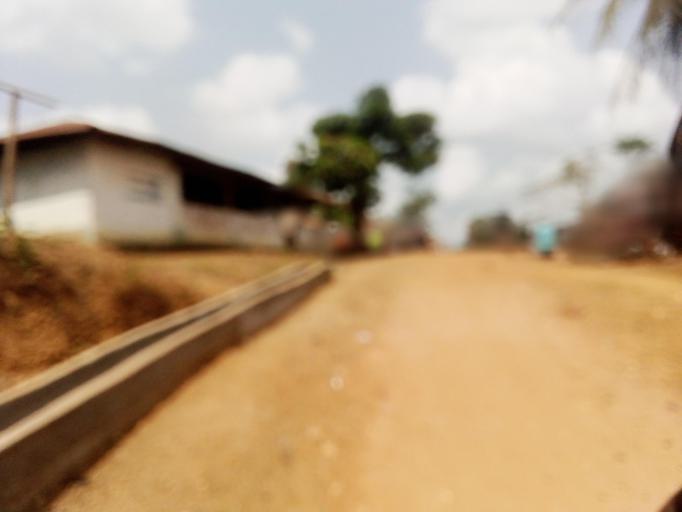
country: SL
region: Southern Province
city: Mogbwemo
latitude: 7.6109
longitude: -12.1861
